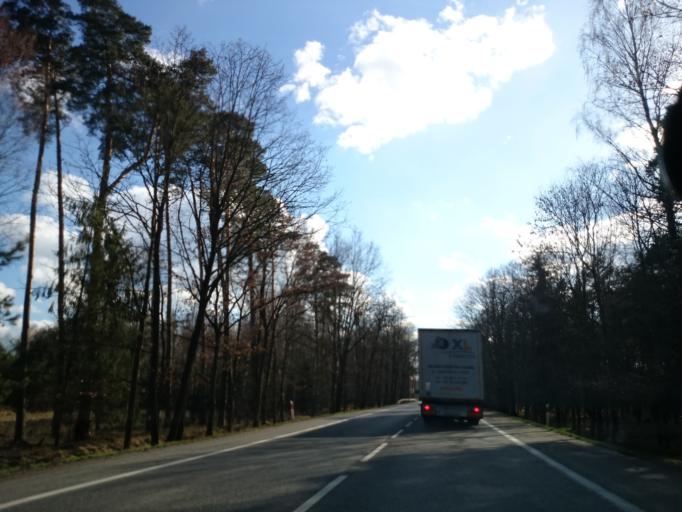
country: PL
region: Opole Voivodeship
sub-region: Powiat opolski
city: Dabrowa
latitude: 50.6698
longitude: 17.7039
